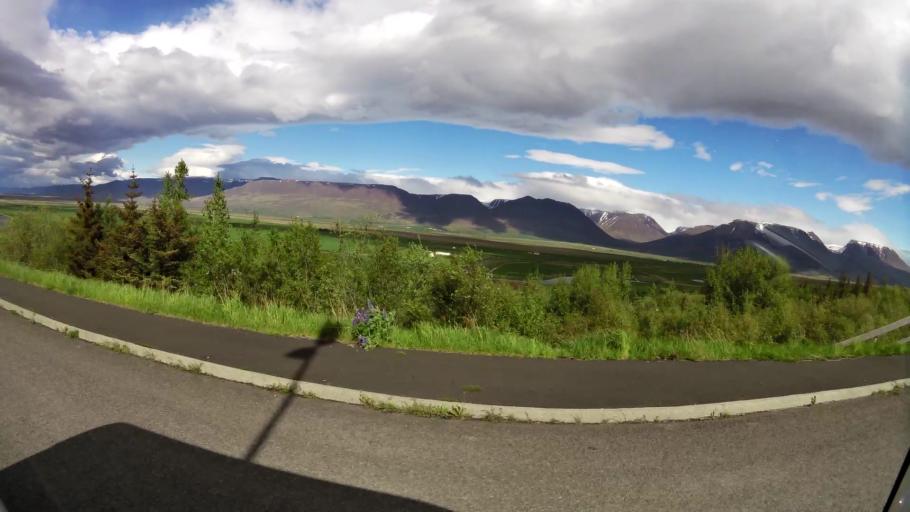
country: IS
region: Northwest
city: Saudarkrokur
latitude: 65.5522
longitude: -19.4491
